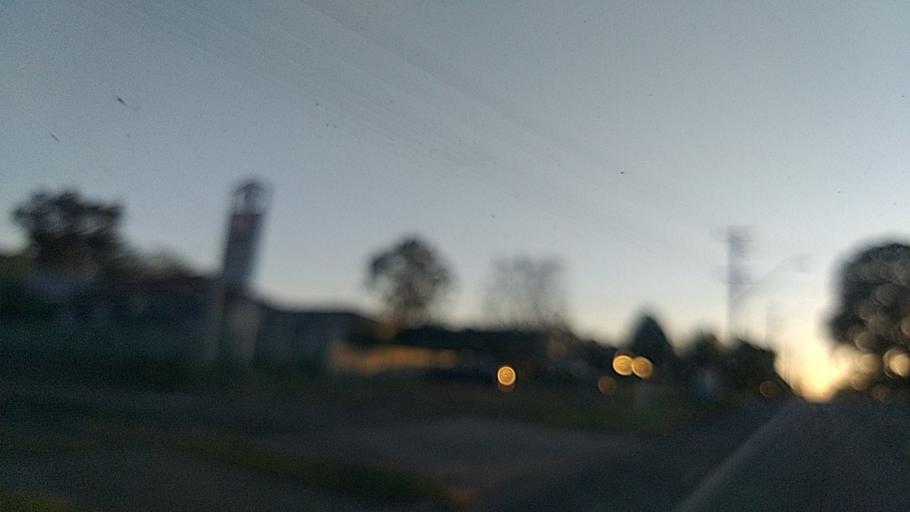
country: AU
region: New South Wales
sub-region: Hawkesbury
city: South Windsor
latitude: -33.6263
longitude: 150.7974
